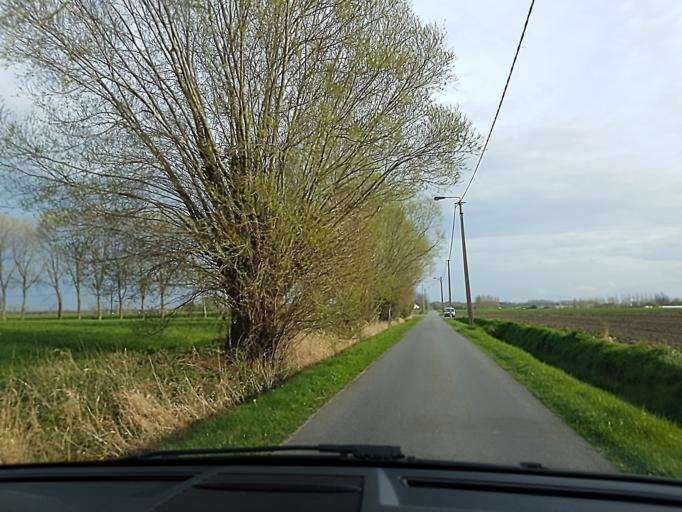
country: BE
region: Flanders
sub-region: Provincie West-Vlaanderen
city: Zedelgem
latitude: 51.1439
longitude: 3.1638
